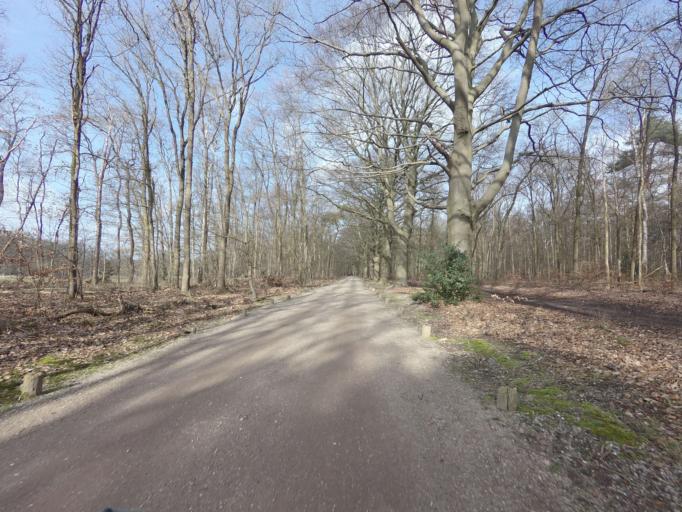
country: NL
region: North Holland
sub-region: Gemeente Bussum
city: Bussum
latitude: 52.2510
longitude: 5.1399
